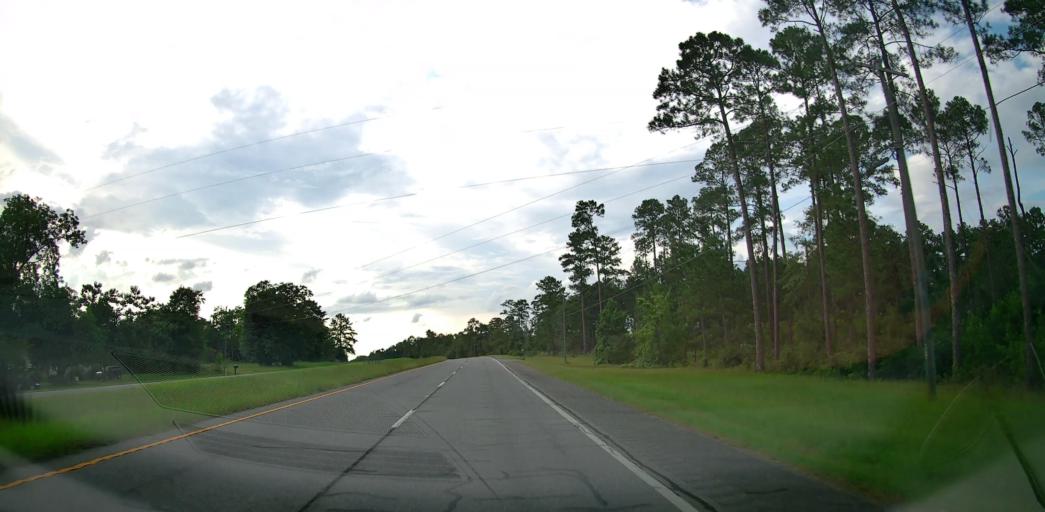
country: US
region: Georgia
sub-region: Pulaski County
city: Hawkinsville
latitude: 32.2668
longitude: -83.4117
